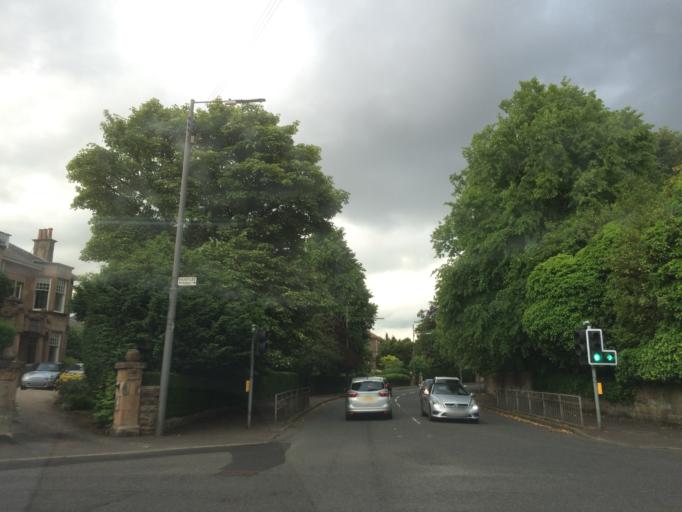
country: GB
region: Scotland
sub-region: East Renfrewshire
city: Giffnock
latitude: 55.8142
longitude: -4.2781
